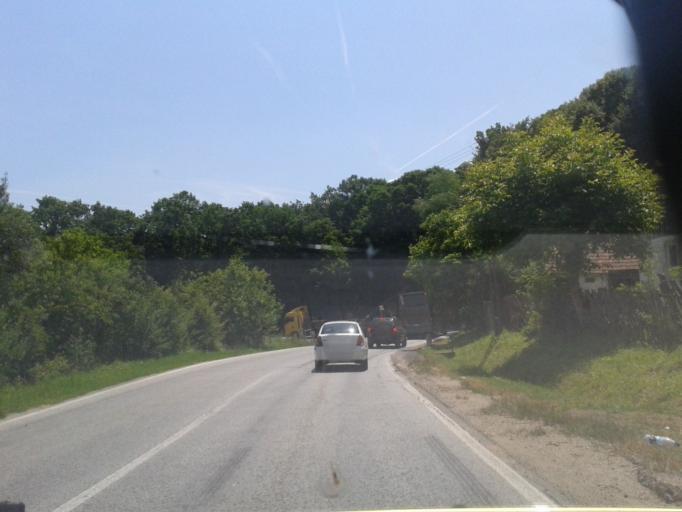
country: RO
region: Hunedoara
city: Lapugiu de Jos
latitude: 45.8856
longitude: 22.4419
